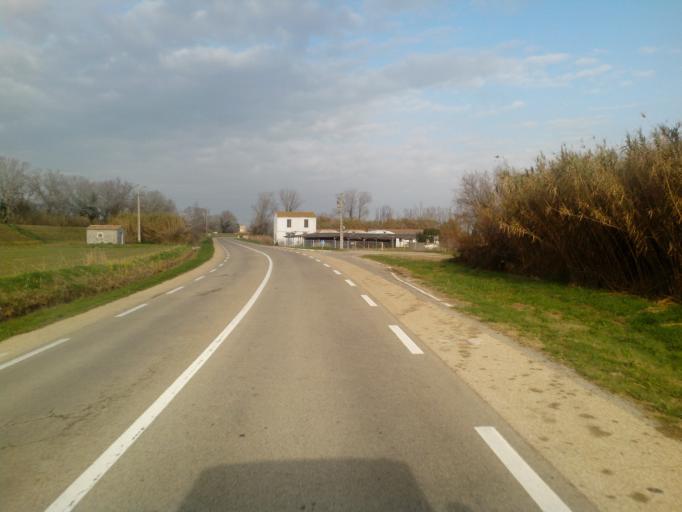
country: FR
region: Languedoc-Roussillon
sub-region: Departement du Gard
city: Saint-Gilles
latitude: 43.6025
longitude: 4.4748
